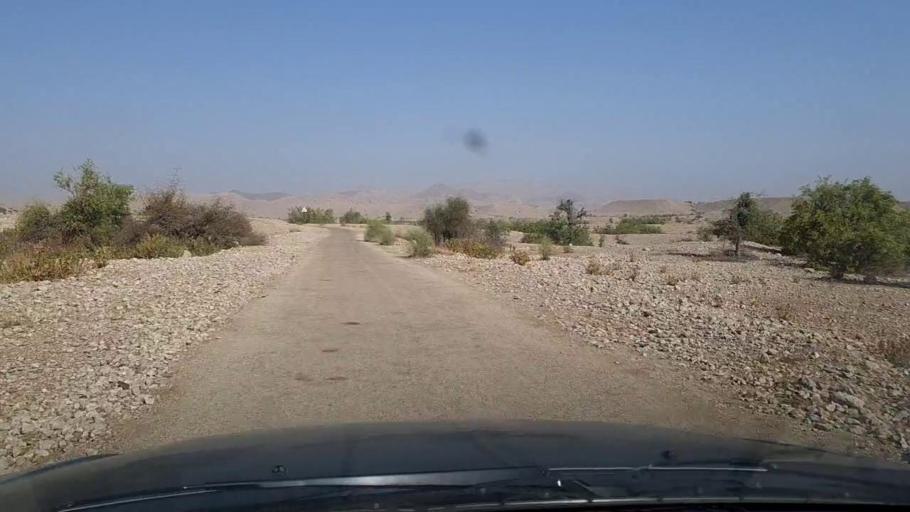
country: PK
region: Sindh
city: Sann
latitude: 25.8791
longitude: 67.9616
